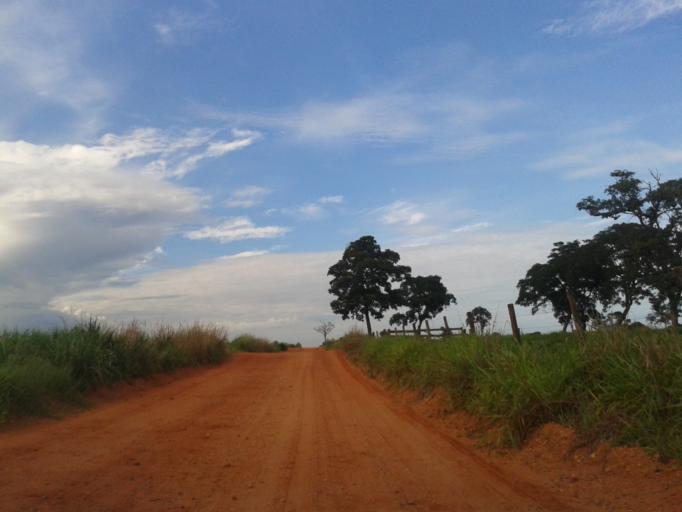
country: BR
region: Minas Gerais
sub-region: Santa Vitoria
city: Santa Vitoria
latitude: -19.0793
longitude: -50.4831
